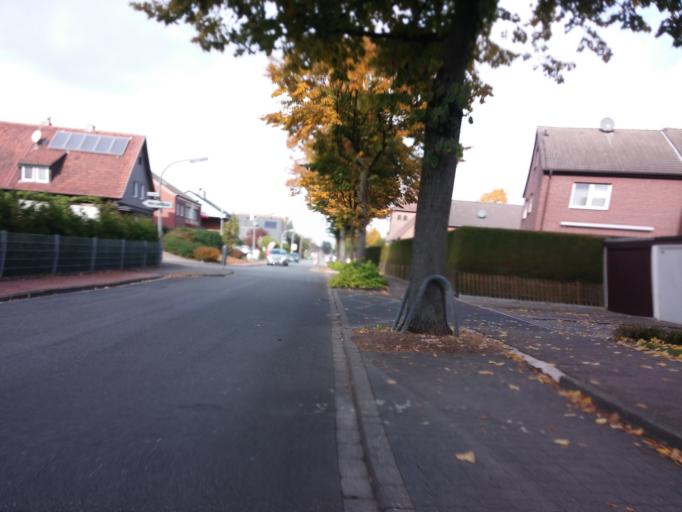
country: DE
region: North Rhine-Westphalia
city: Dorsten
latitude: 51.6360
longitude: 7.0128
